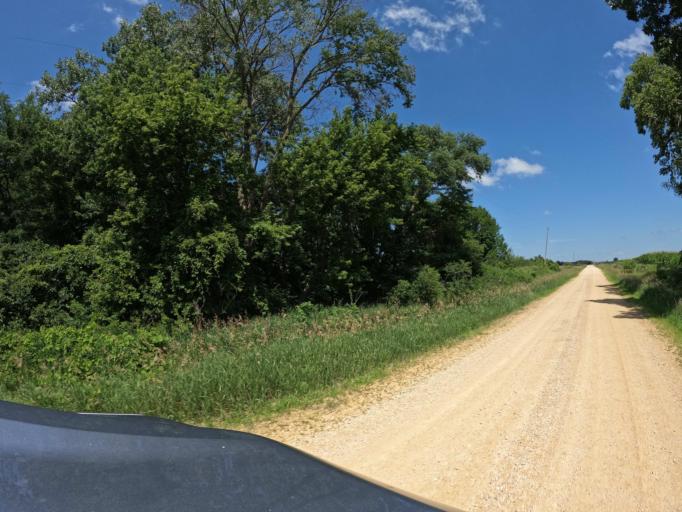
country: US
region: Iowa
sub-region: Clinton County
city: De Witt
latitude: 41.7669
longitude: -90.4325
